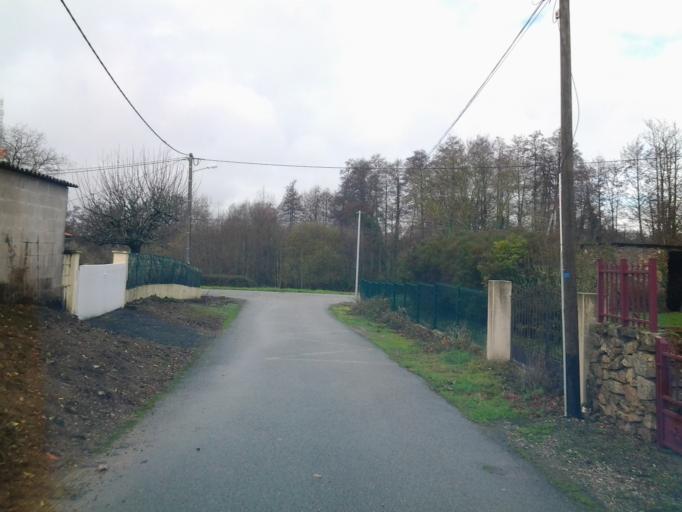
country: FR
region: Pays de la Loire
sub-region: Departement de la Vendee
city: La Ferriere
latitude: 46.6799
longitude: -1.3556
